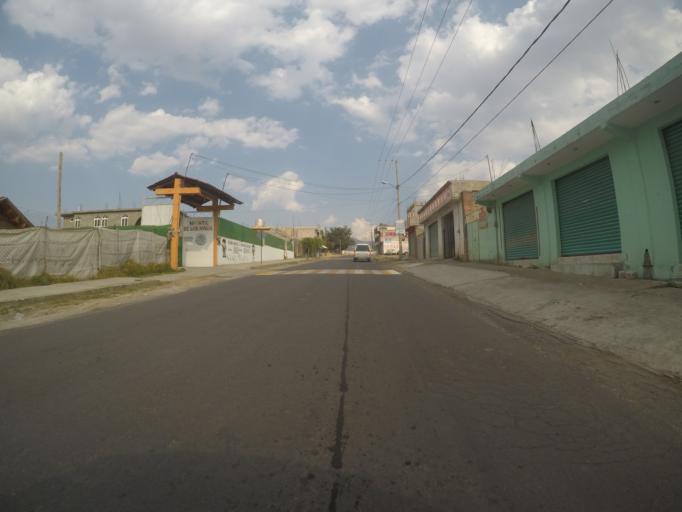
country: MX
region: Mexico
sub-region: Xalatlaco
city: Techichili
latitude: 19.1743
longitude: -99.4214
